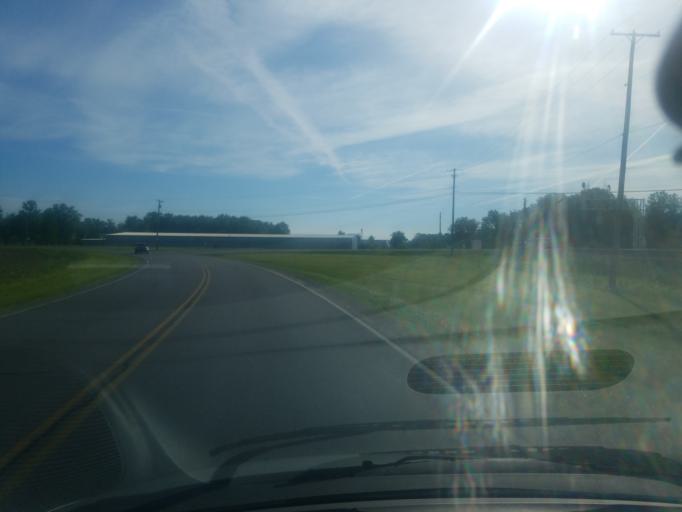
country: US
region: Ohio
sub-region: Marion County
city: Marion
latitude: 40.6047
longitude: -83.0746
